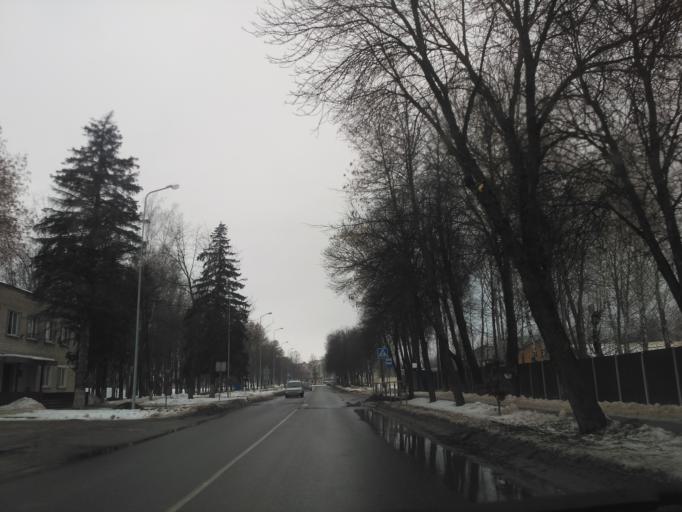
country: BY
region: Minsk
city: Horad Zhodzina
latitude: 54.0948
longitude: 28.3341
